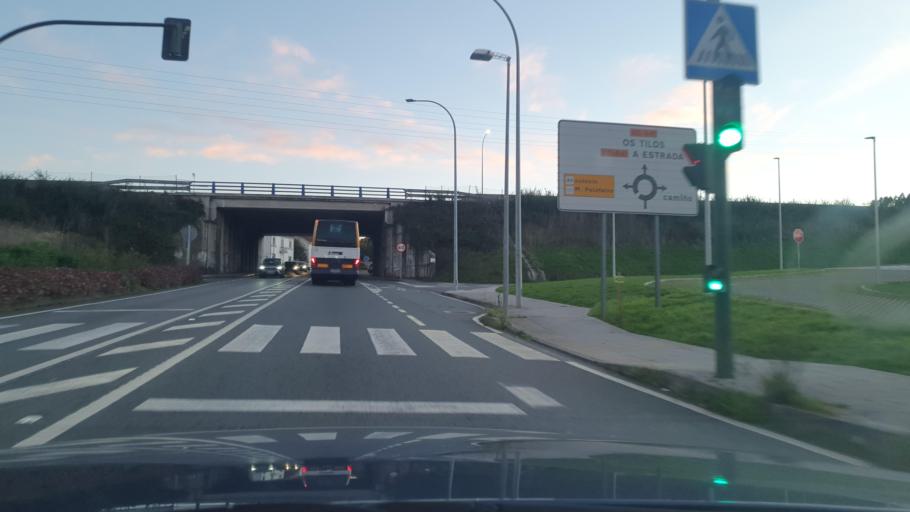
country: ES
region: Galicia
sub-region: Provincia da Coruna
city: Santiago de Compostela
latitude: 42.8539
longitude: -8.5393
